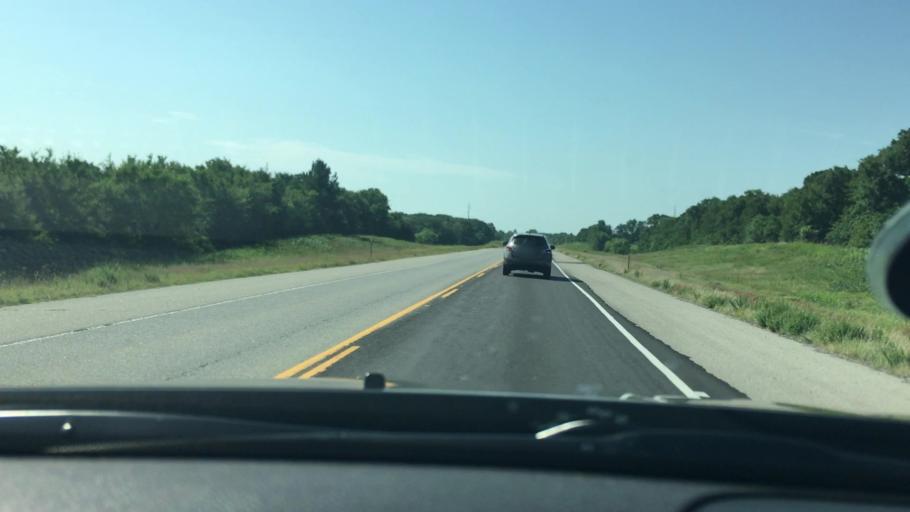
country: US
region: Oklahoma
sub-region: Pontotoc County
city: Ada
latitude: 34.6576
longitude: -96.5591
